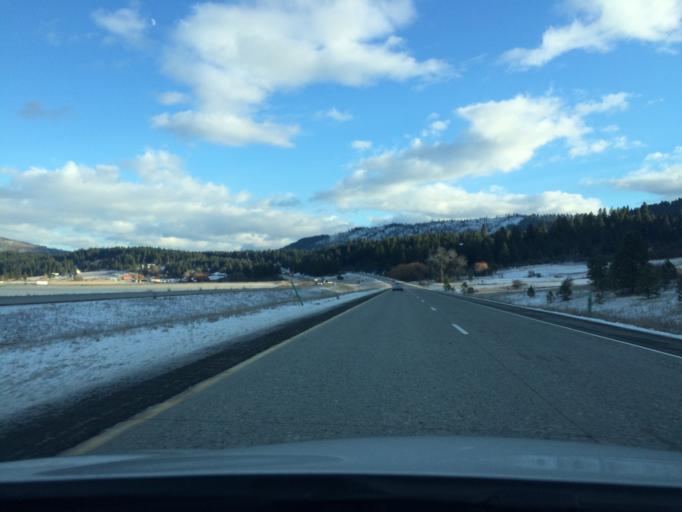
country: US
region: Washington
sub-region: Kittitas County
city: Cle Elum
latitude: 47.1670
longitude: -120.8791
